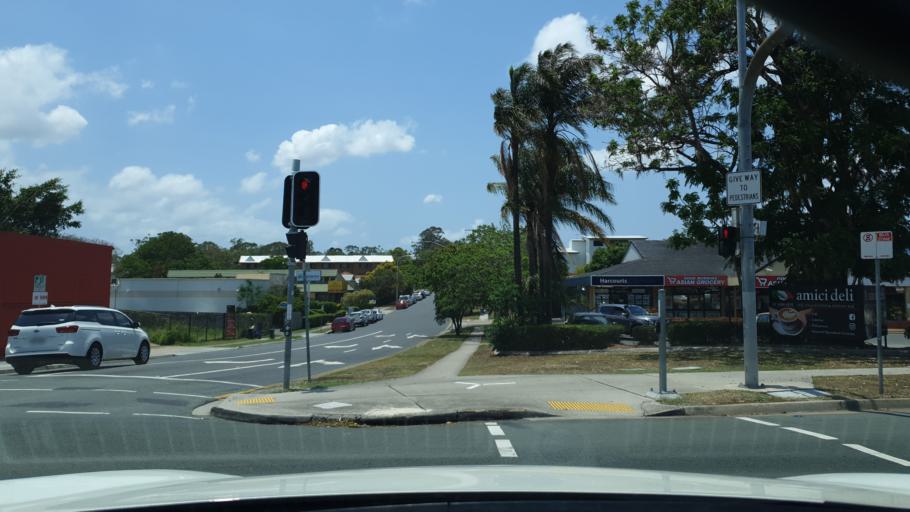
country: AU
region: Queensland
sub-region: Brisbane
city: Wavell Heights
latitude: -27.3899
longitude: 153.0315
